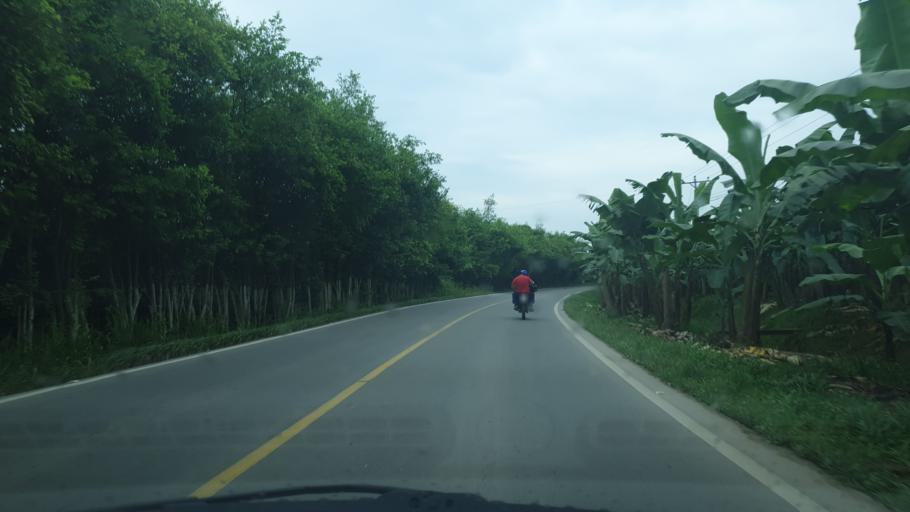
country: EC
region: El Oro
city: Pasaje
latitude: -3.3610
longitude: -79.8368
